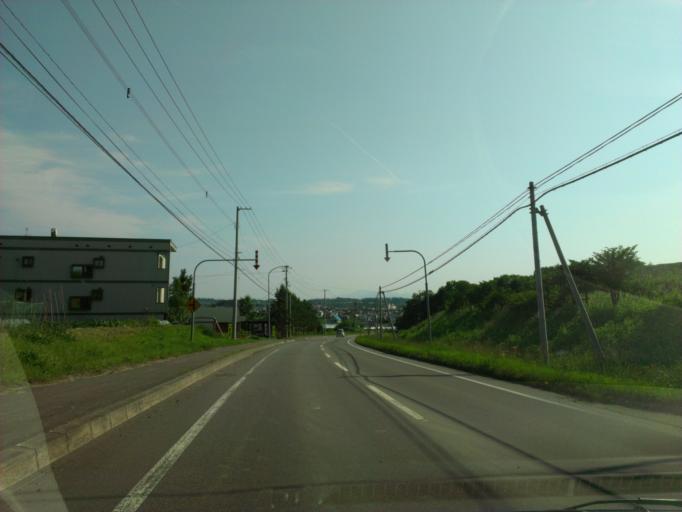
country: JP
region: Hokkaido
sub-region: Asahikawa-shi
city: Asahikawa
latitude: 43.6024
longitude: 142.4765
